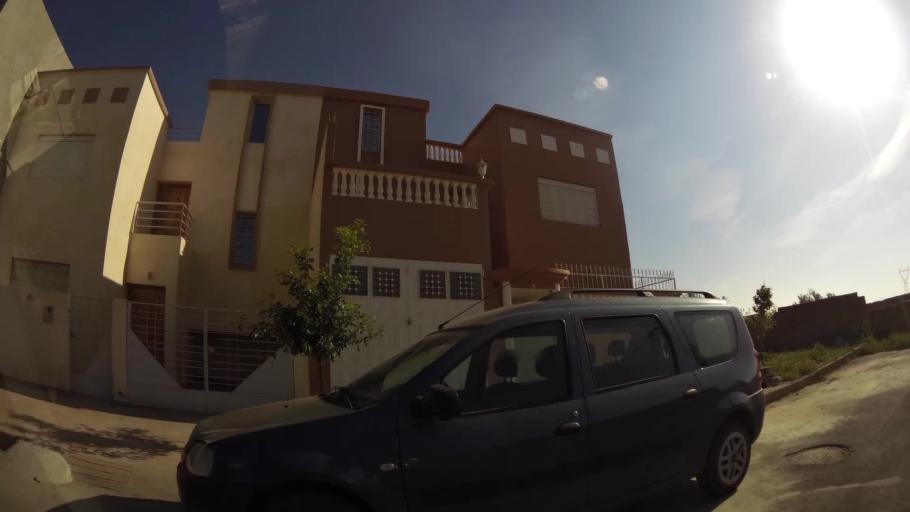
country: MA
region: Oriental
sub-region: Oujda-Angad
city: Oujda
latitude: 34.7223
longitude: -1.8878
